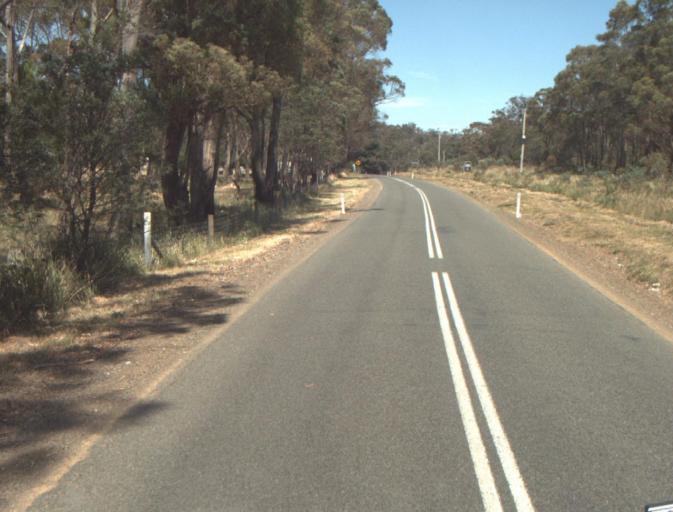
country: AU
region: Tasmania
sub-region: Launceston
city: Mayfield
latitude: -41.3369
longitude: 147.1432
